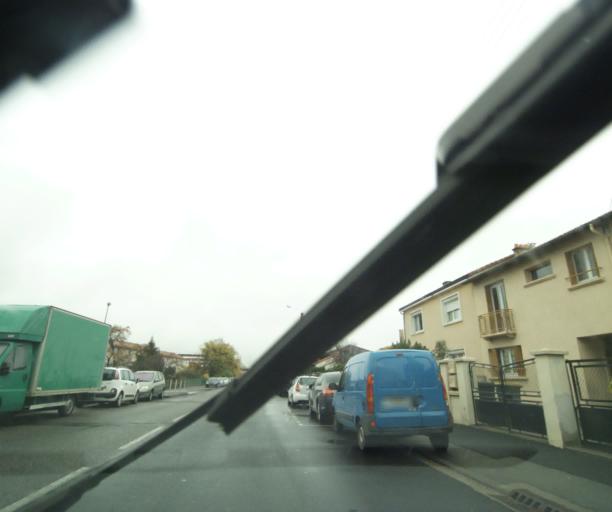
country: FR
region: Auvergne
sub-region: Departement du Puy-de-Dome
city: Aubiere
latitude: 45.7617
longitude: 3.1050
